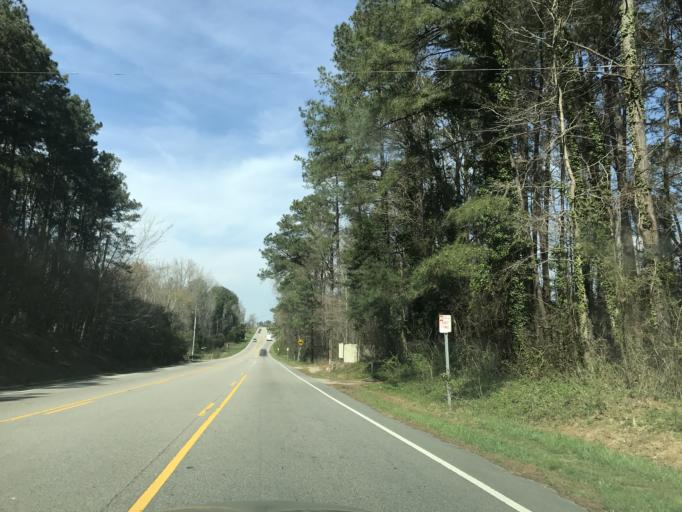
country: US
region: North Carolina
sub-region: Wake County
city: Knightdale
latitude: 35.8380
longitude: -78.5433
